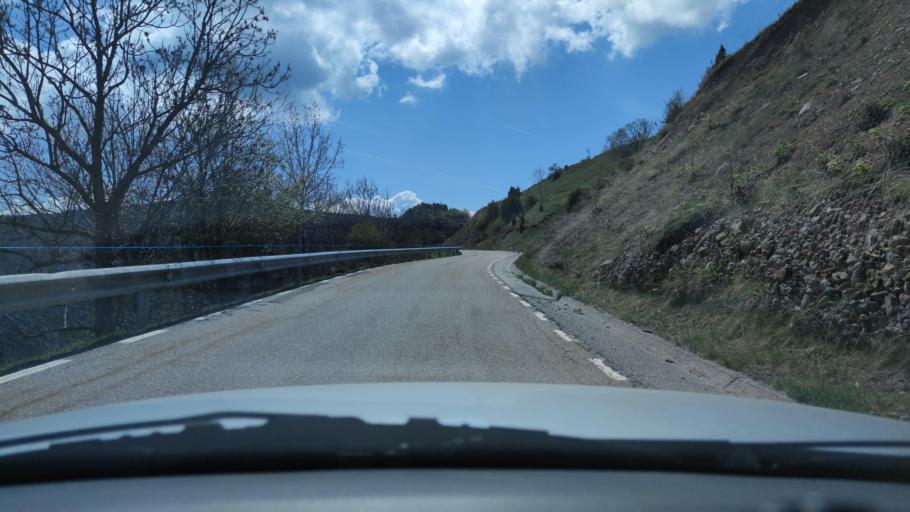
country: ES
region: Catalonia
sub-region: Provincia de Lleida
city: Coll de Nargo
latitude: 42.2895
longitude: 1.2313
